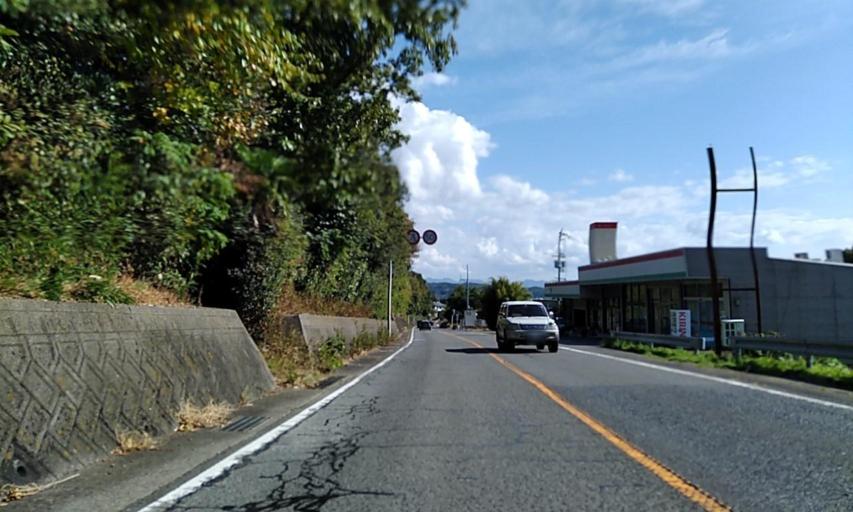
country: JP
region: Wakayama
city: Tanabe
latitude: 33.7795
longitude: 135.3059
